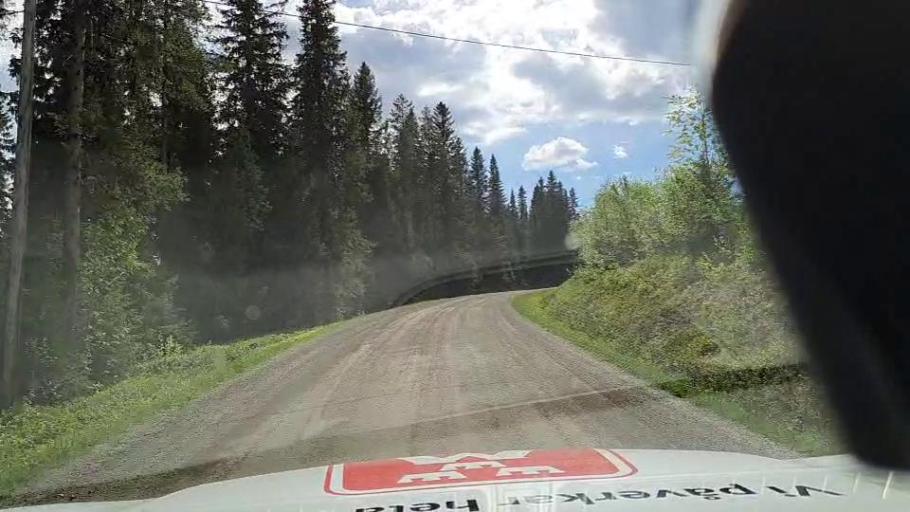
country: SE
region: Vaesterbotten
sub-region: Vilhelmina Kommun
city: Sjoberg
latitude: 64.5625
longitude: 15.8481
